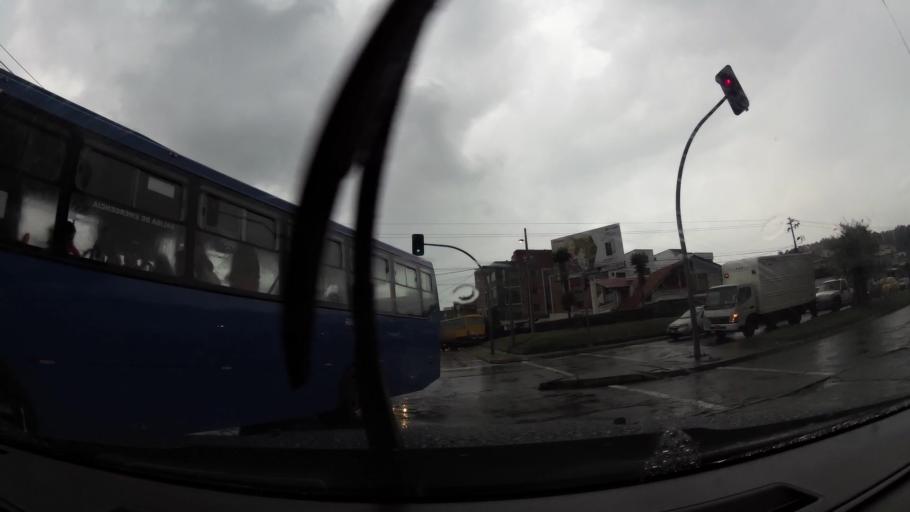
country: EC
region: Pichincha
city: Quito
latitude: -0.1596
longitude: -78.4638
